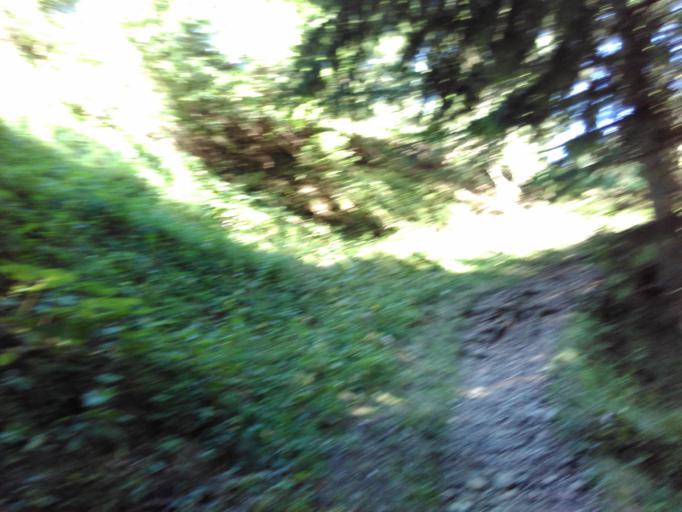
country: CH
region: Lucerne
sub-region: Lucerne-Land District
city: Vitznau
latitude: 47.0476
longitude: 8.4769
